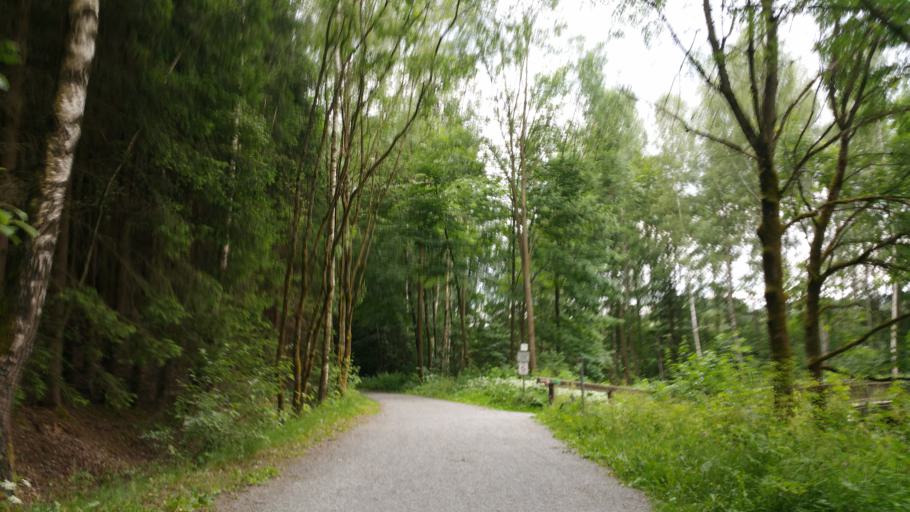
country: DE
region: Bavaria
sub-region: Upper Franconia
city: Oberkotzau
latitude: 50.2718
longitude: 11.9096
